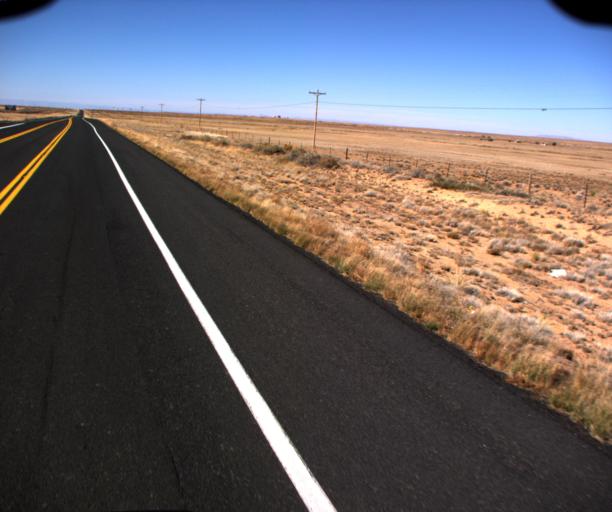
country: US
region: Arizona
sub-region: Coconino County
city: Tuba City
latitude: 35.9981
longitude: -111.0308
